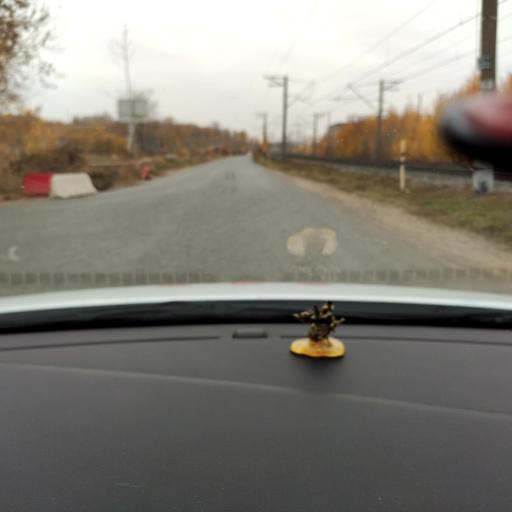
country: RU
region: Tatarstan
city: Verkhniy Uslon
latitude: 55.8038
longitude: 49.0329
